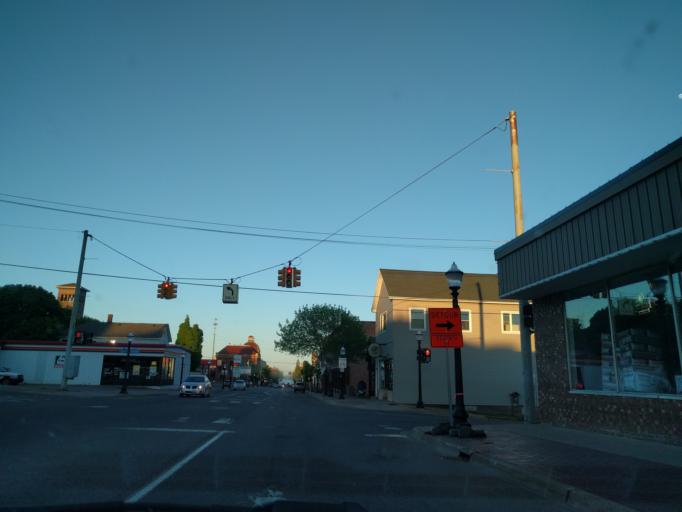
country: US
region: Michigan
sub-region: Marquette County
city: Marquette
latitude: 46.5443
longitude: -87.4002
